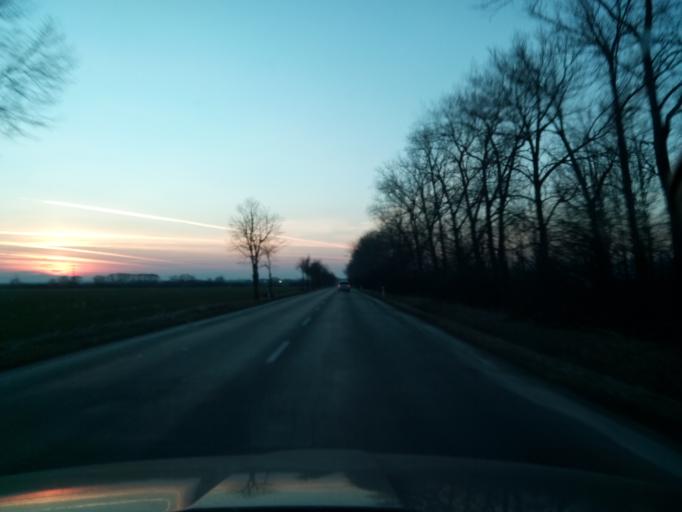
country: SK
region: Kosicky
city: Sobrance
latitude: 48.7619
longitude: 22.1165
